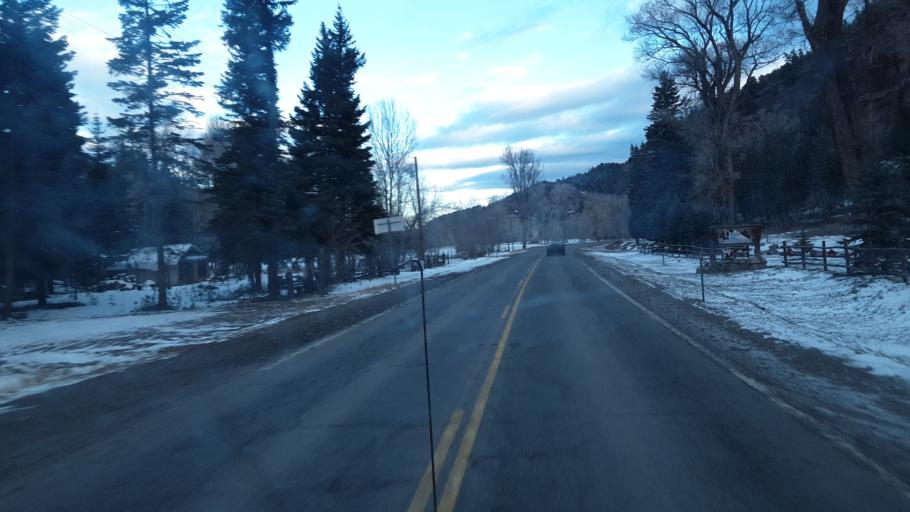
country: US
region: Colorado
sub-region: Ouray County
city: Ouray
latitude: 38.0438
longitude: -107.6814
